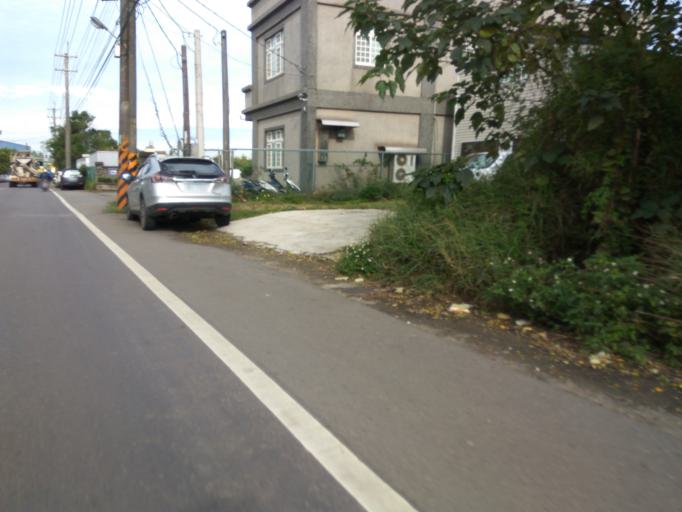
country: TW
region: Taiwan
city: Daxi
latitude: 24.9393
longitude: 121.1604
